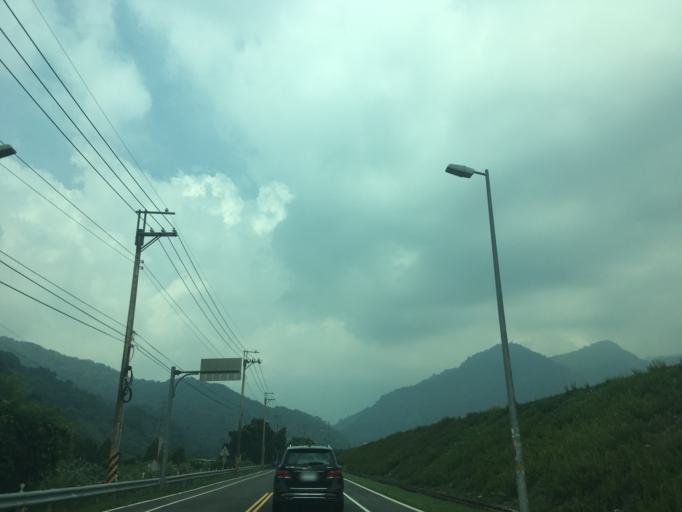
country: TW
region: Taiwan
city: Fengyuan
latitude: 24.2962
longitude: 120.8886
